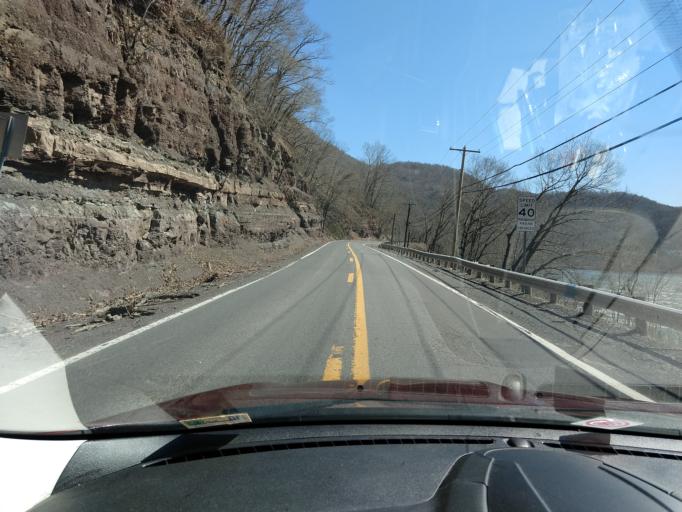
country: US
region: West Virginia
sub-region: Summers County
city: Hinton
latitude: 37.6958
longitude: -80.8790
